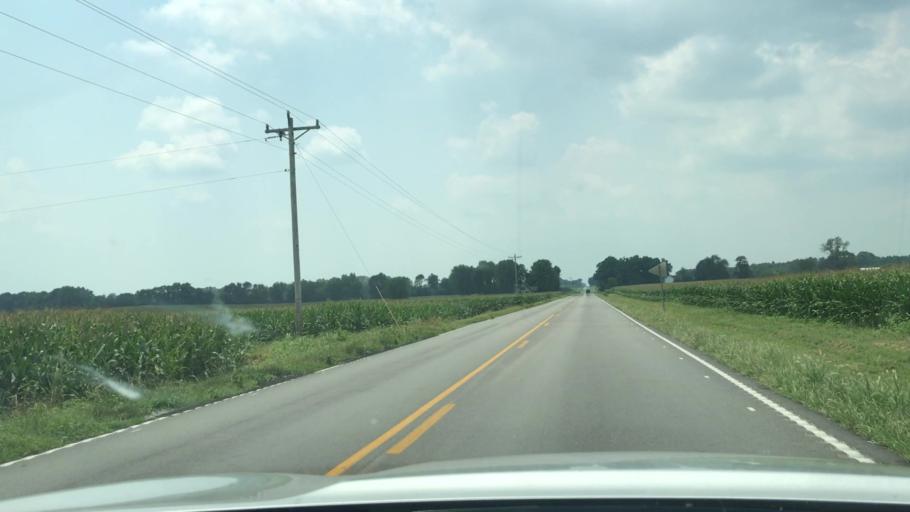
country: US
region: Kentucky
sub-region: Todd County
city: Guthrie
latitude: 36.6987
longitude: -87.1192
